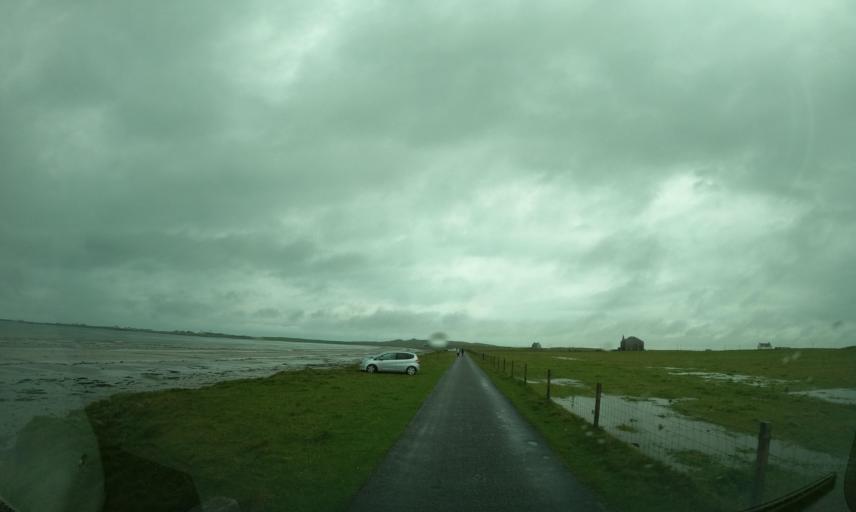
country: GB
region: Scotland
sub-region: Eilean Siar
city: Barra
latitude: 56.5210
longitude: -6.8092
